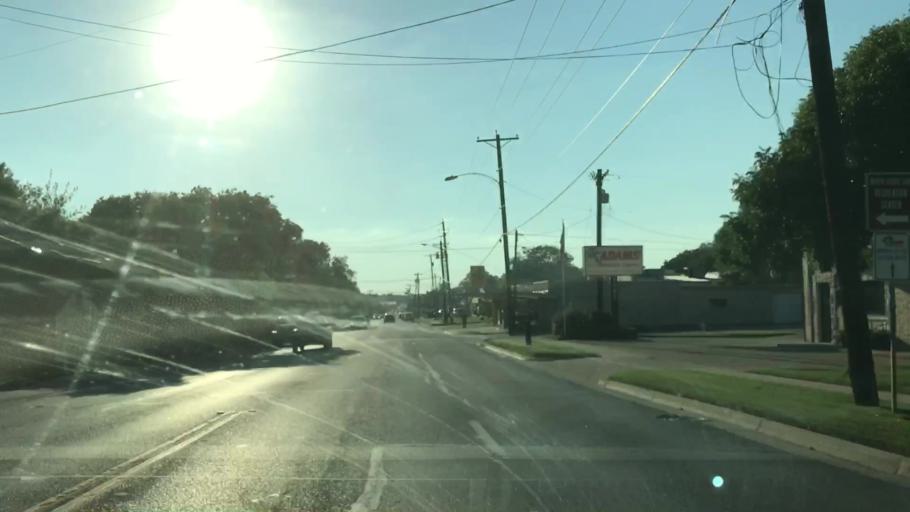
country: US
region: Texas
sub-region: Denton County
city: Denton
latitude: 33.2160
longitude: -97.1170
